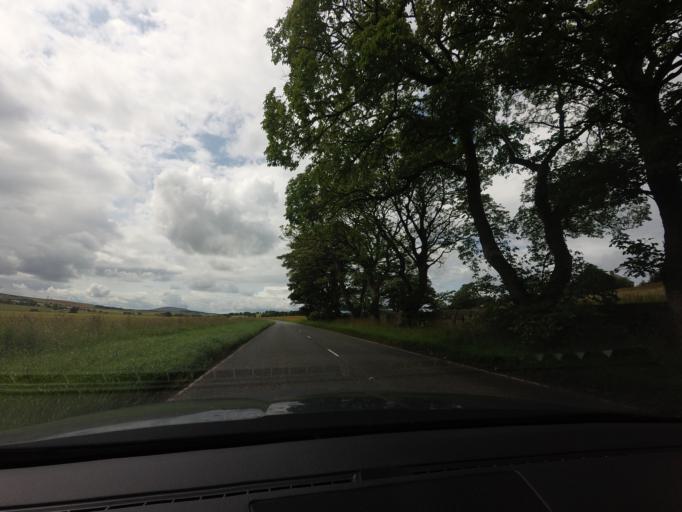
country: GB
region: Scotland
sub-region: Aberdeenshire
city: Whitehills
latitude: 57.6611
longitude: -2.5904
